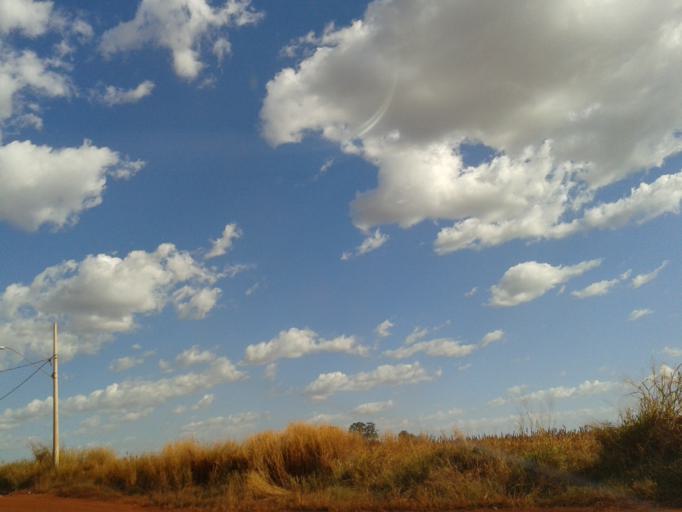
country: BR
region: Minas Gerais
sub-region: Capinopolis
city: Capinopolis
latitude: -18.6979
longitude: -49.5705
